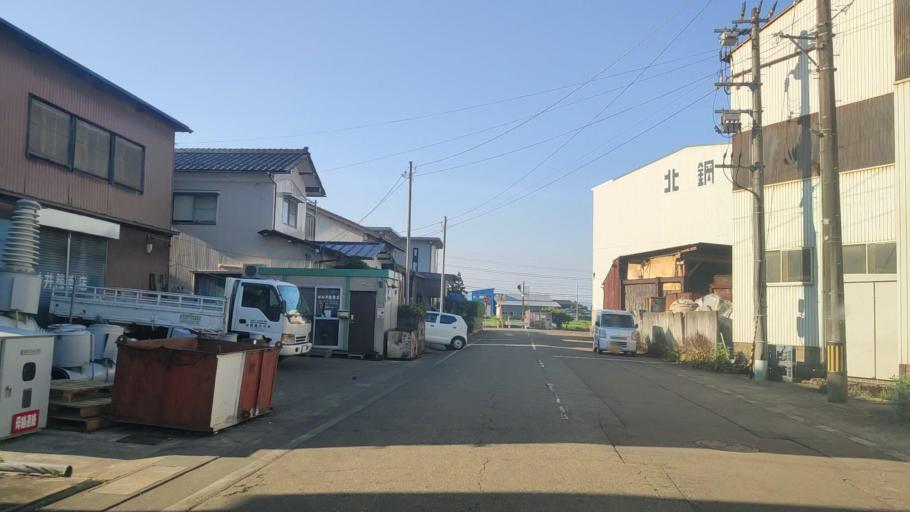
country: JP
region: Fukui
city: Fukui-shi
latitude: 36.0841
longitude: 136.2630
